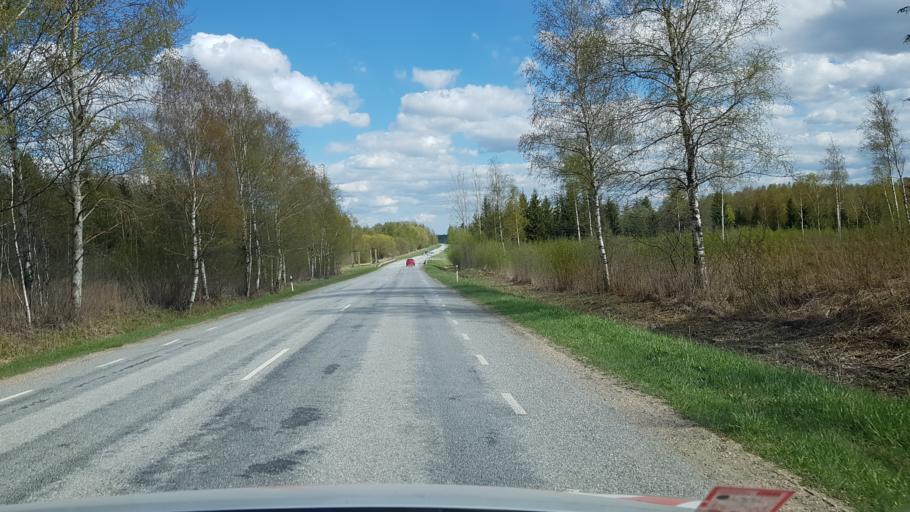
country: EE
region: Tartu
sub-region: UElenurme vald
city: Ulenurme
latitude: 58.3305
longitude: 26.7303
